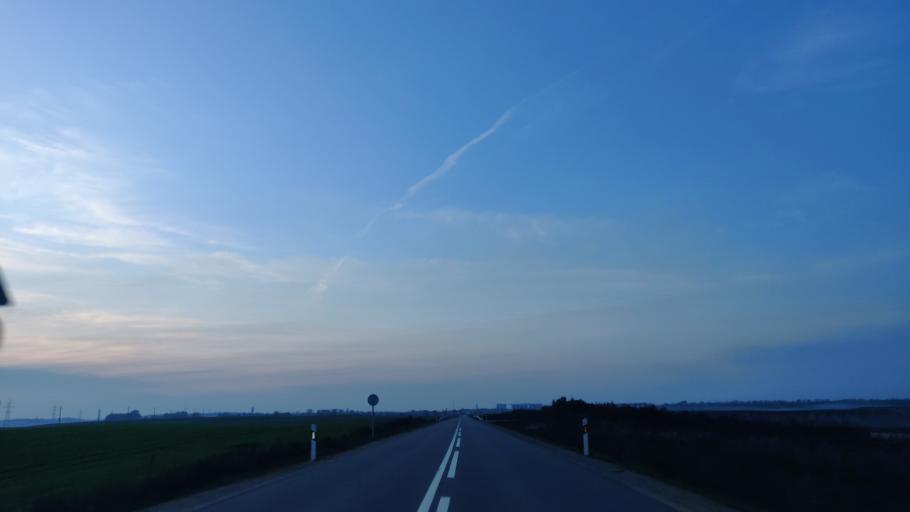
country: LT
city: Lentvaris
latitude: 54.6020
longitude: 25.0077
